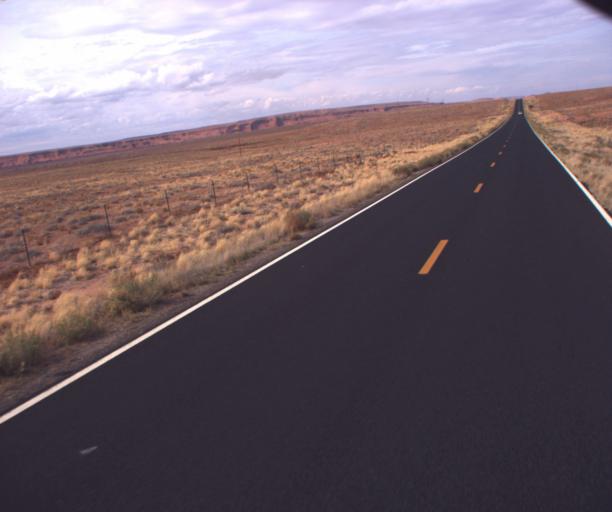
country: US
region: Arizona
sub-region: Apache County
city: Many Farms
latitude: 36.5769
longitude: -109.5520
